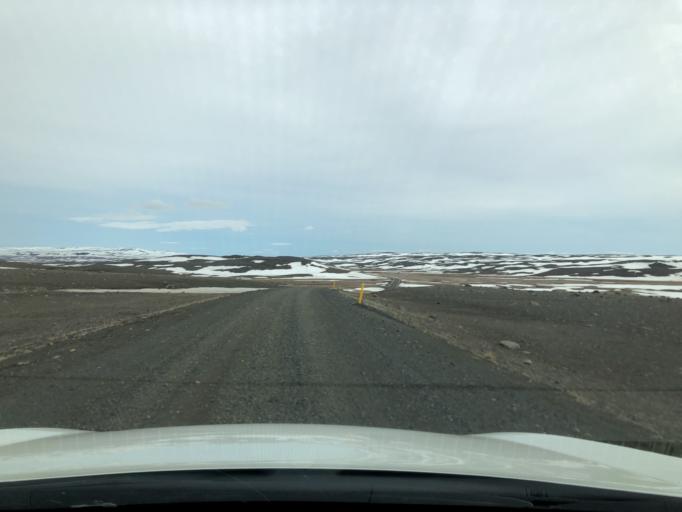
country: IS
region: East
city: Egilsstadir
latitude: 65.2936
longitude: -15.4506
